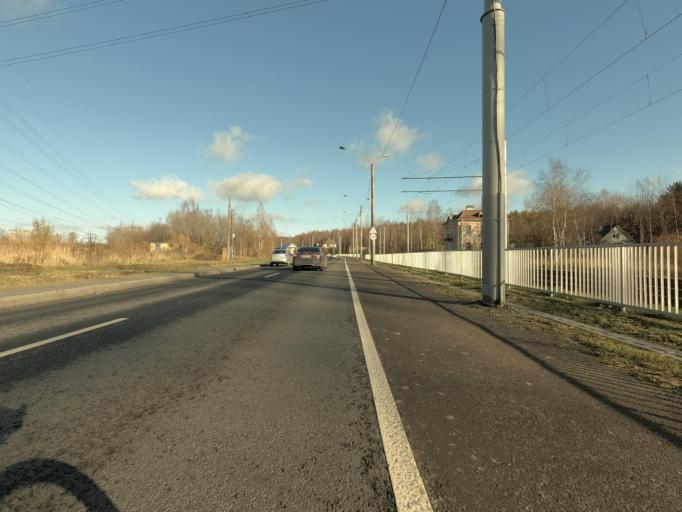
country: RU
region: St.-Petersburg
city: Krasnogvargeisky
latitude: 59.9646
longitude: 30.4981
